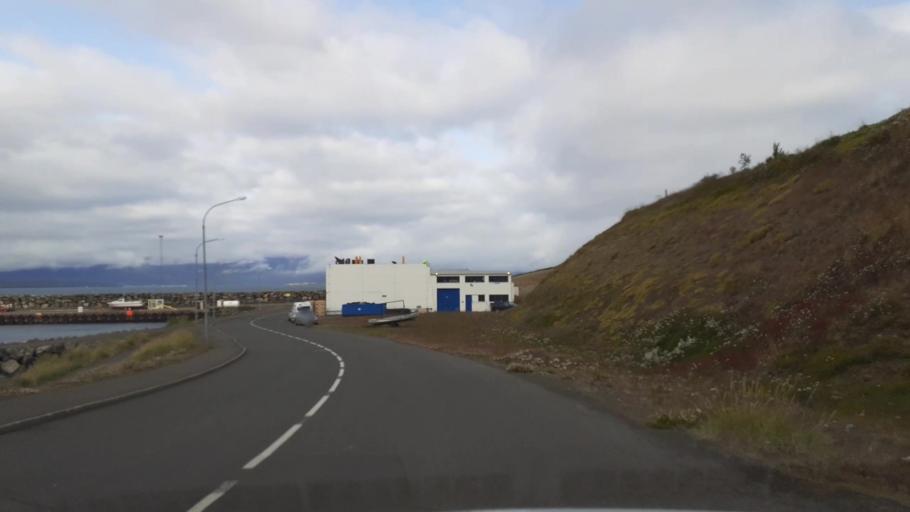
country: IS
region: Northeast
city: Akureyri
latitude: 65.9537
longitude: -18.1817
